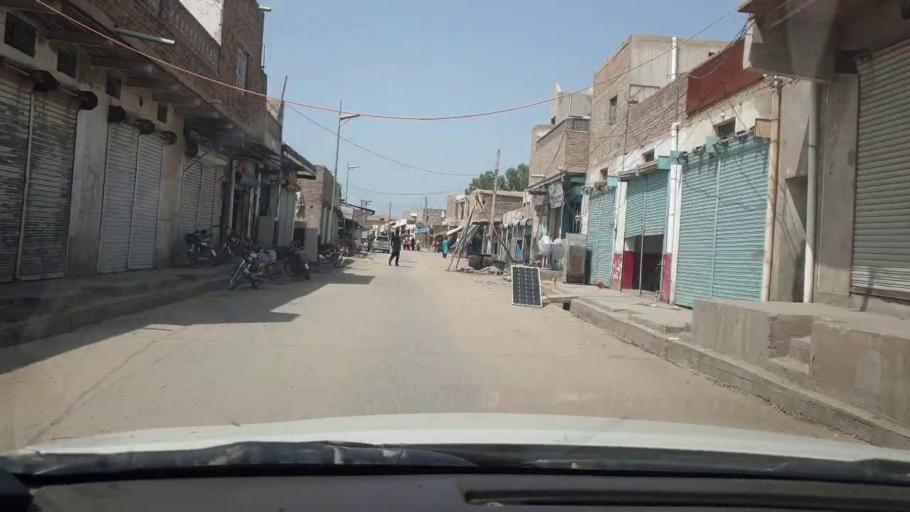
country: PK
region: Sindh
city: Rohri
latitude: 27.5136
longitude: 69.0442
